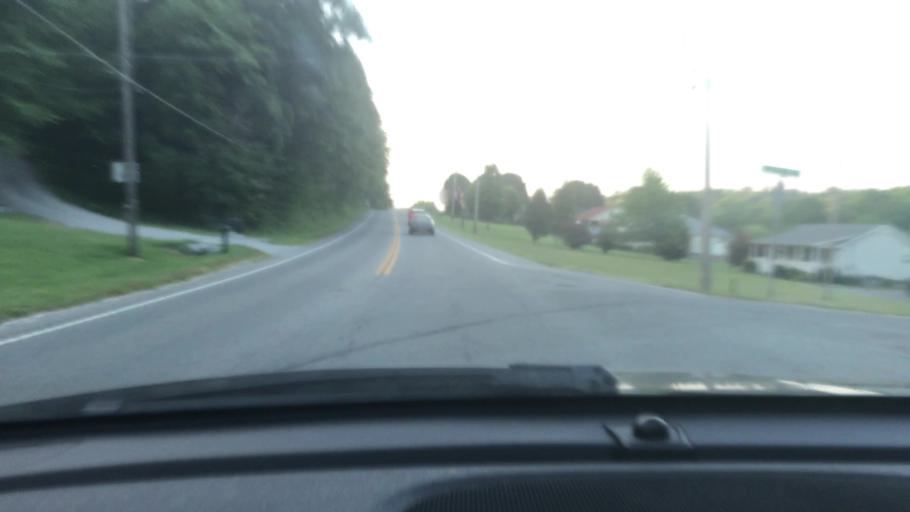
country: US
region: Tennessee
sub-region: Dickson County
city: Dickson
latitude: 36.1223
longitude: -87.3608
